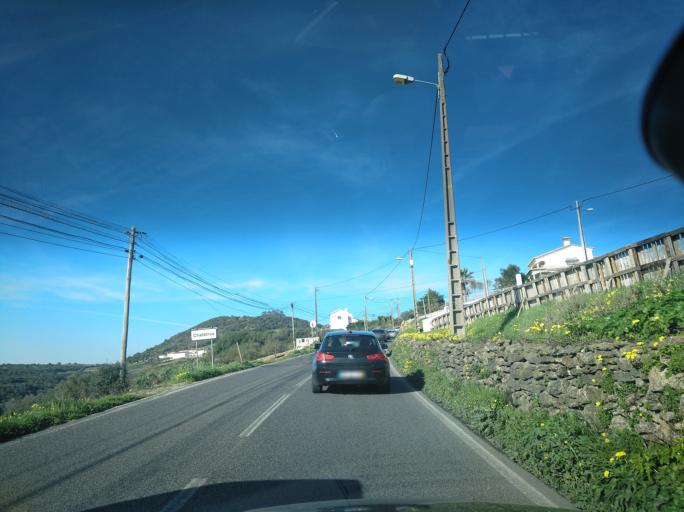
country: PT
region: Lisbon
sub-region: Sintra
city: Pero Pinheiro
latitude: 38.8914
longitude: -9.3271
